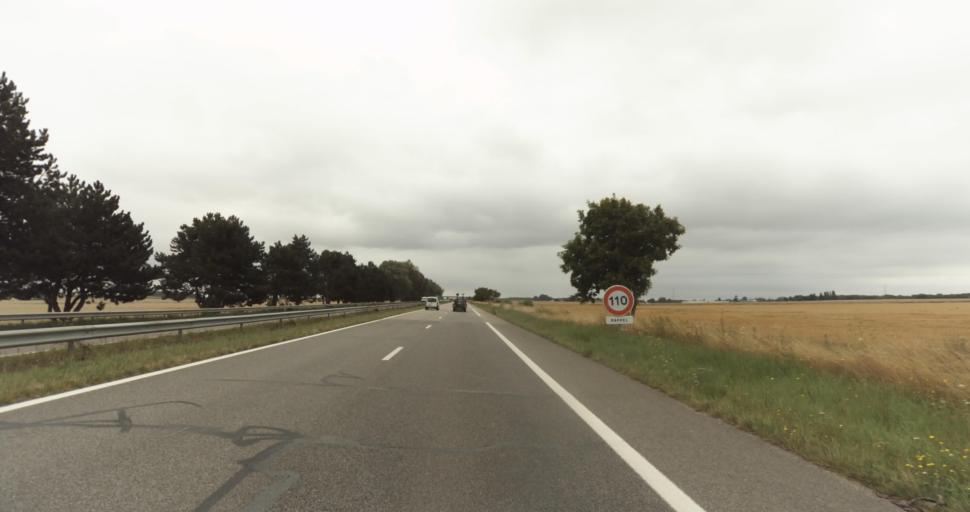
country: FR
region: Haute-Normandie
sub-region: Departement de l'Eure
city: Normanville
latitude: 49.0923
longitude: 1.1885
